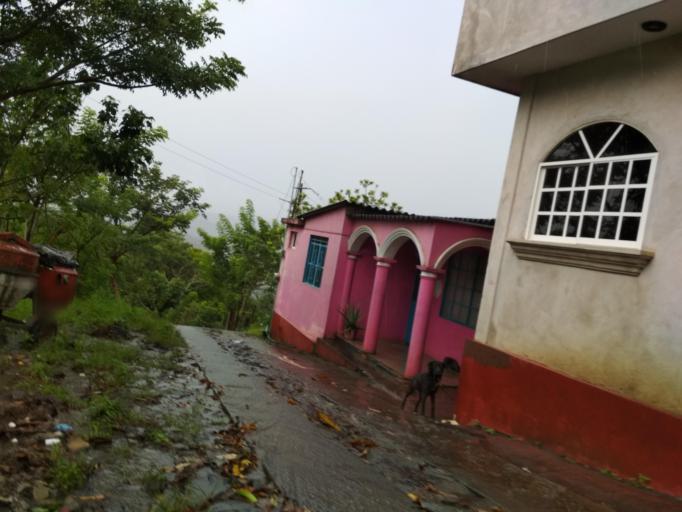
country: MX
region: Veracruz
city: Santiago Tuxtla
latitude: 18.4619
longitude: -95.2924
